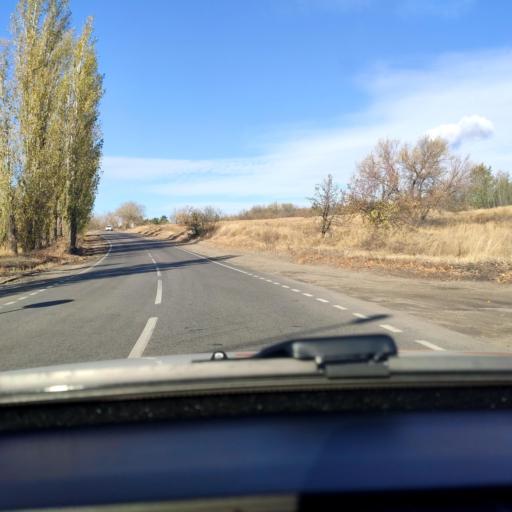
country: RU
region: Voronezj
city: Shilovo
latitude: 51.5514
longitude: 39.1346
